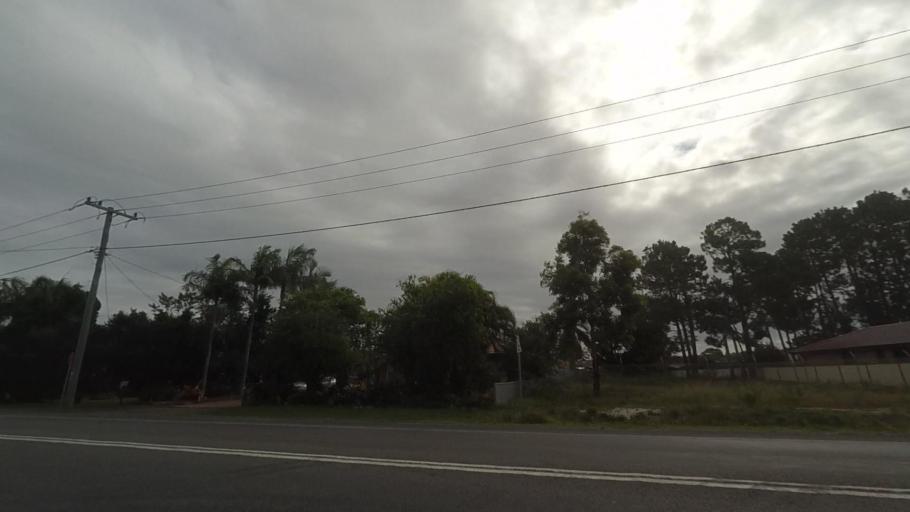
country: AU
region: New South Wales
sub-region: Great Lakes
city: Hawks Nest
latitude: -32.6529
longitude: 152.1494
